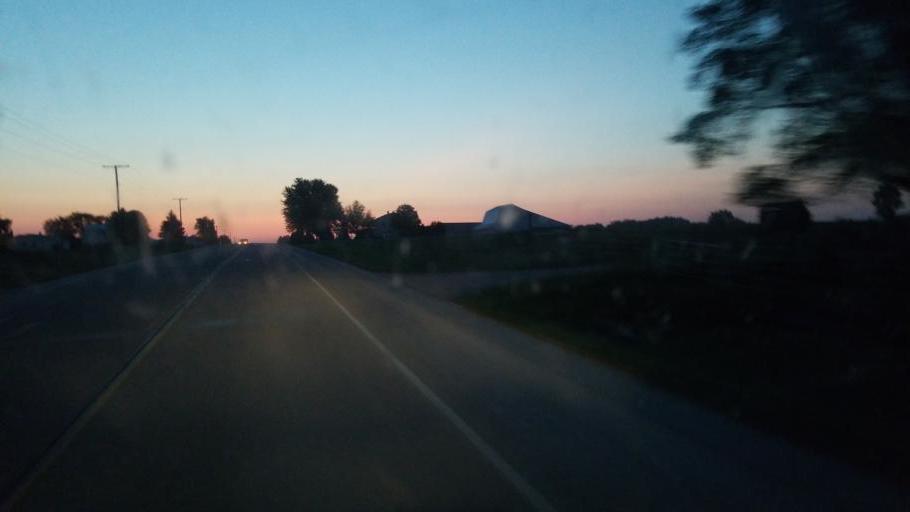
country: US
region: Indiana
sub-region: Elkhart County
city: Middlebury
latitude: 41.6759
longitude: -85.6264
